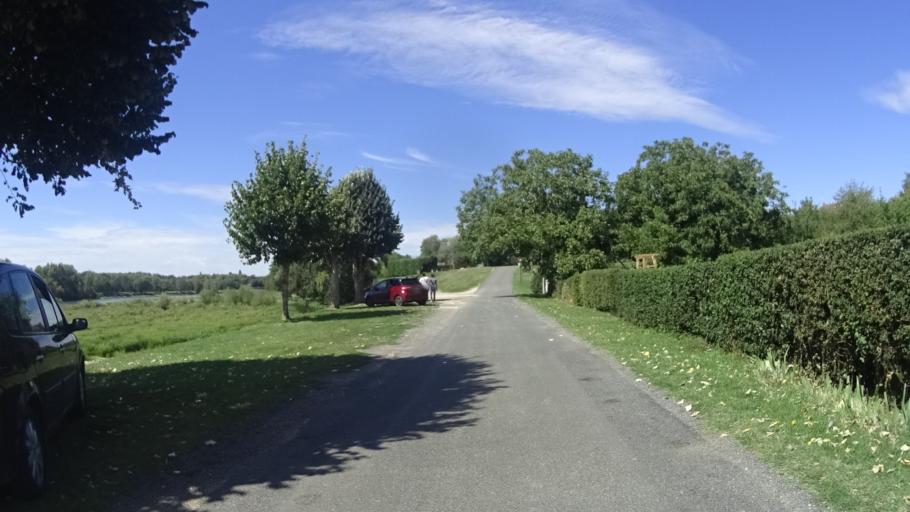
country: FR
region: Centre
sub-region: Departement du Loiret
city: Briare
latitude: 47.5897
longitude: 2.7814
